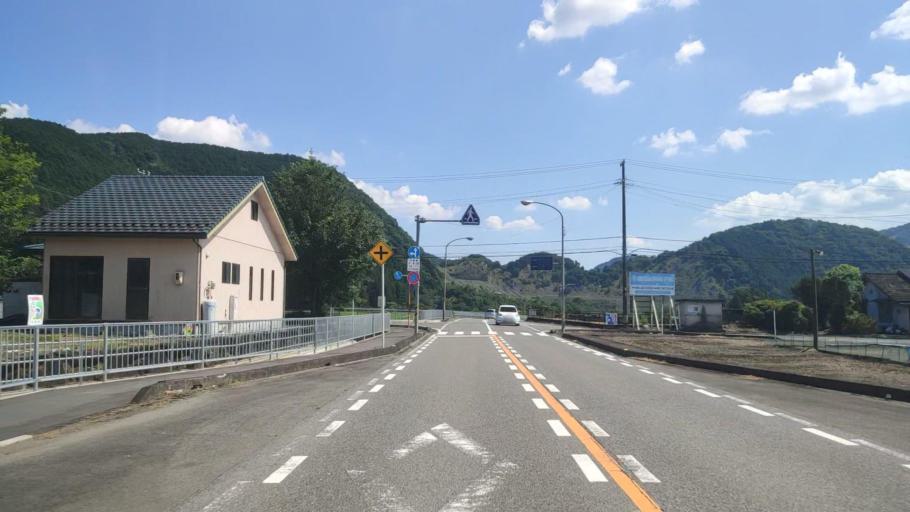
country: JP
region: Gifu
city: Godo
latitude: 35.5344
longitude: 136.6512
